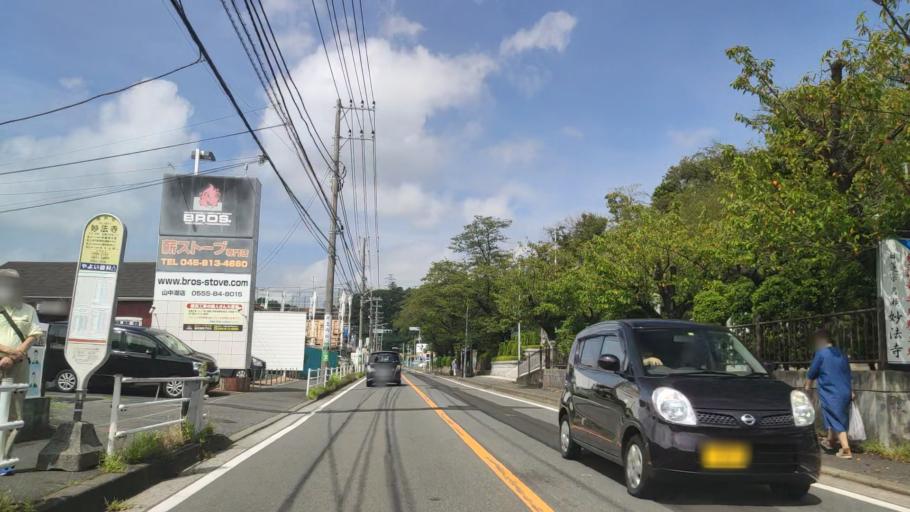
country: JP
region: Kanagawa
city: Yokohama
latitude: 35.4292
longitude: 139.5402
